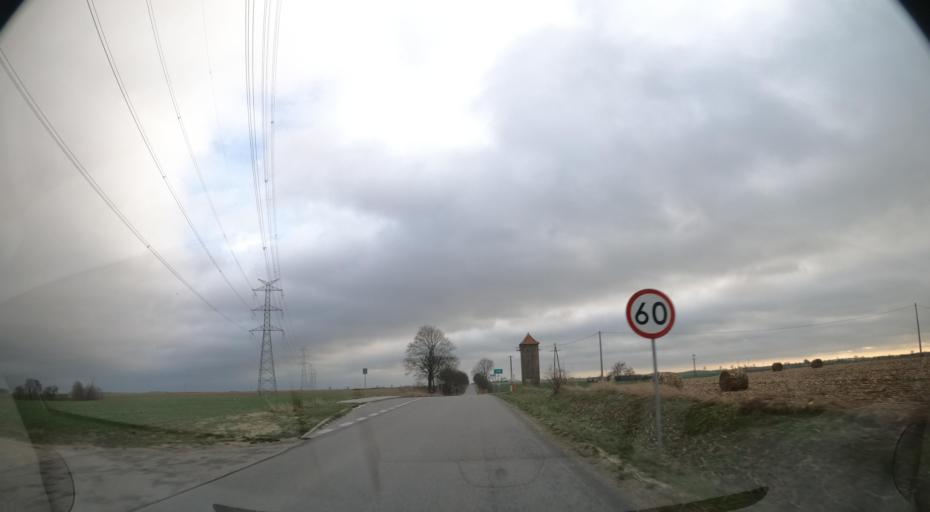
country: PL
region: Kujawsko-Pomorskie
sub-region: Powiat nakielski
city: Sadki
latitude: 53.1778
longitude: 17.4149
